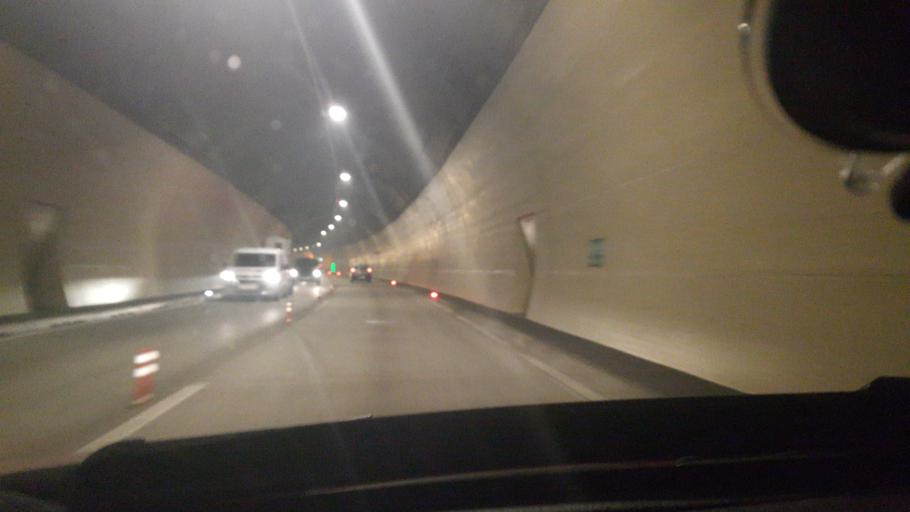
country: AT
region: Carinthia
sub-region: Klagenfurt am Woerthersee
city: Klagenfurt am Woerthersee
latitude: 46.6547
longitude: 14.3065
